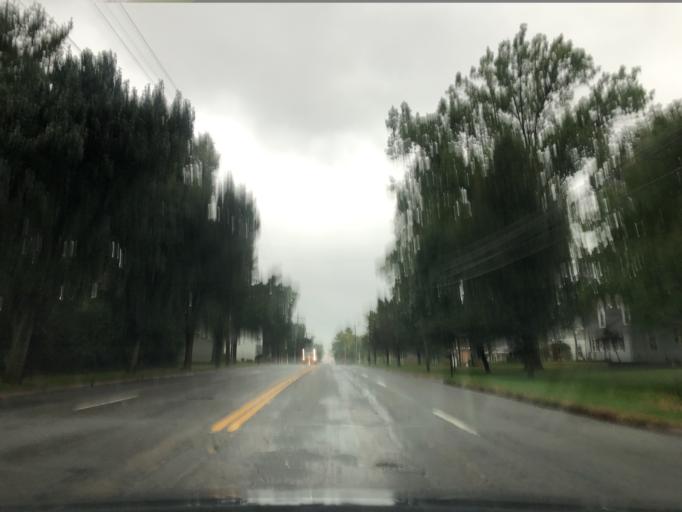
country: US
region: Ohio
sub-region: Hamilton County
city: Blue Ash
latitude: 39.2224
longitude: -84.3779
